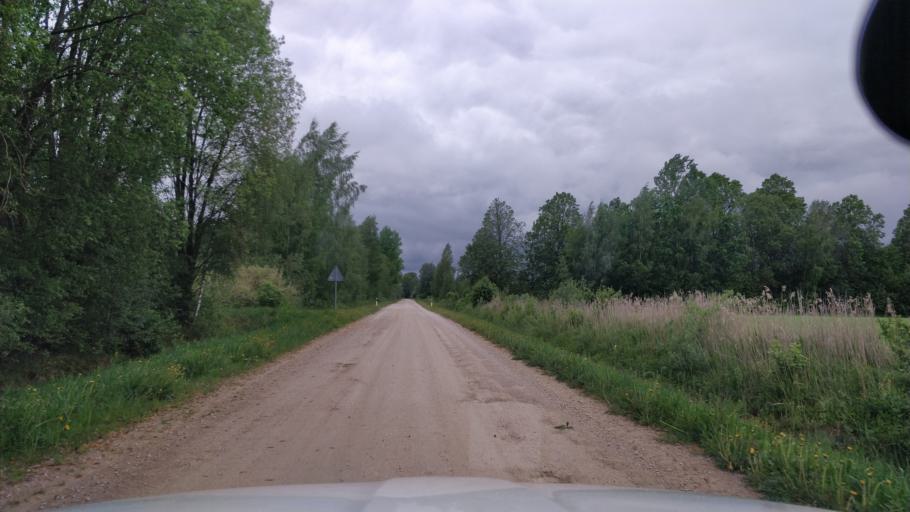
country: EE
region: Raplamaa
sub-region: Maerjamaa vald
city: Marjamaa
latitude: 58.7156
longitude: 24.3083
